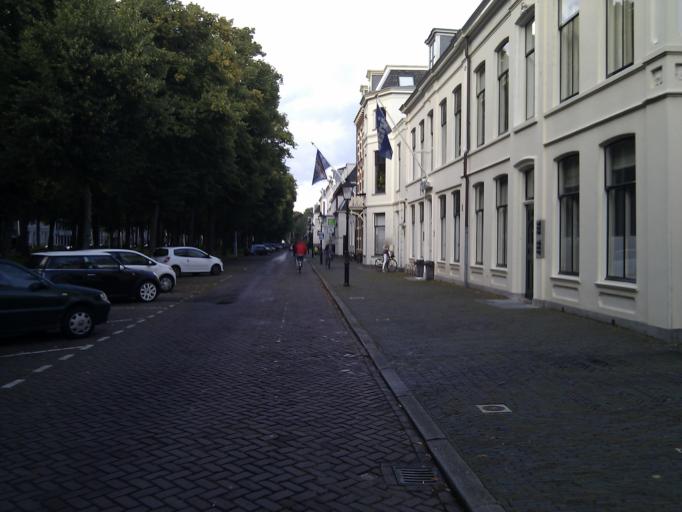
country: NL
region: Utrecht
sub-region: Gemeente Utrecht
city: Utrecht
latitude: 52.0915
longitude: 5.1342
